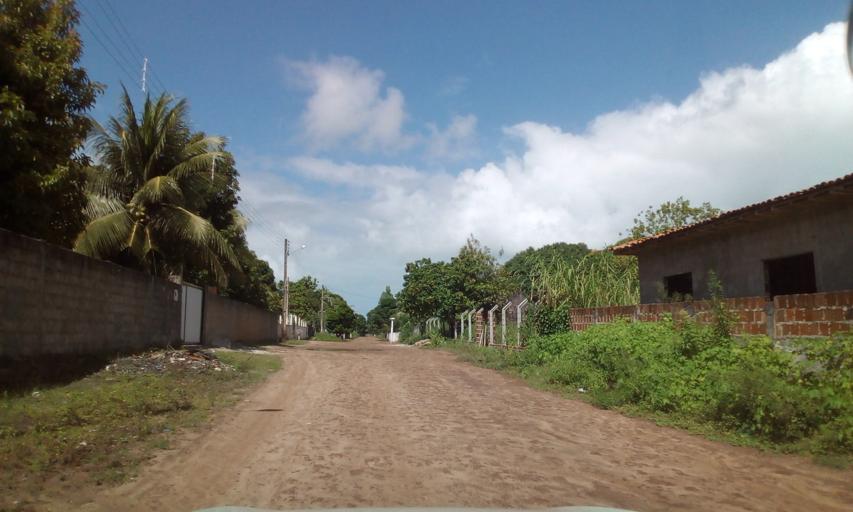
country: BR
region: Paraiba
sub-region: Conde
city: Conde
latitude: -7.2195
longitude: -34.8226
